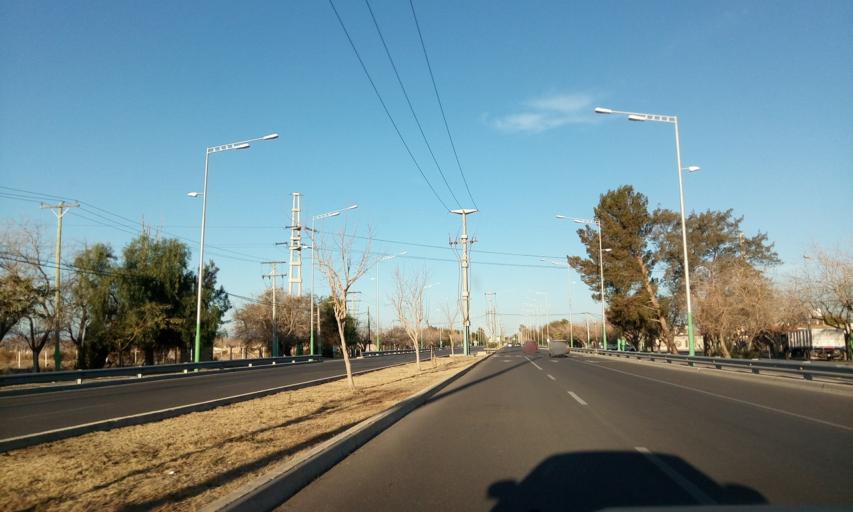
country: AR
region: San Juan
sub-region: Departamento de Rivadavia
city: Rivadavia
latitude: -31.5285
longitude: -68.6044
